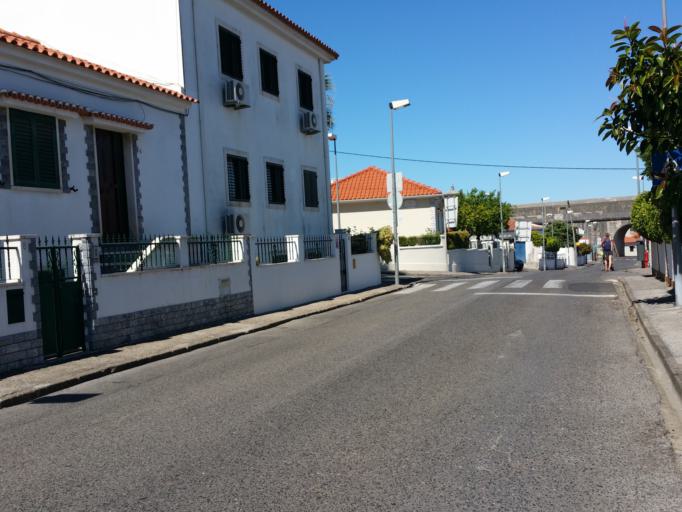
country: PT
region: Lisbon
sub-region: Lisbon
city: Lisbon
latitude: 38.7319
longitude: -9.1736
